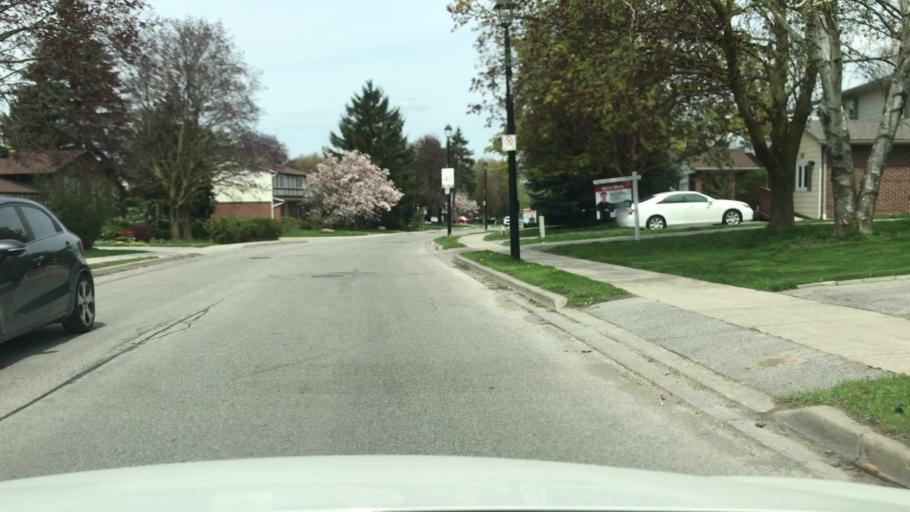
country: CA
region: Ontario
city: Newmarket
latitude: 44.0417
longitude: -79.4697
